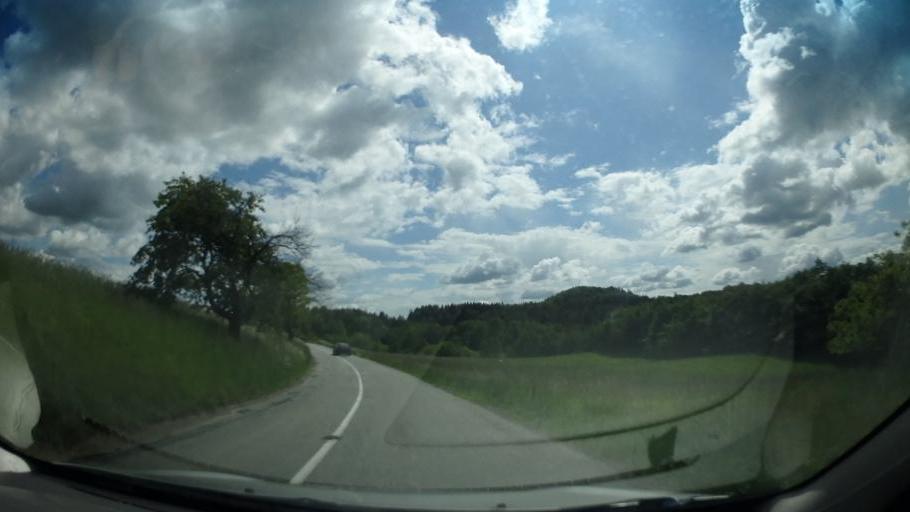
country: CZ
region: South Moravian
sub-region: Okres Blansko
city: Letovice
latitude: 49.6090
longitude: 16.6074
